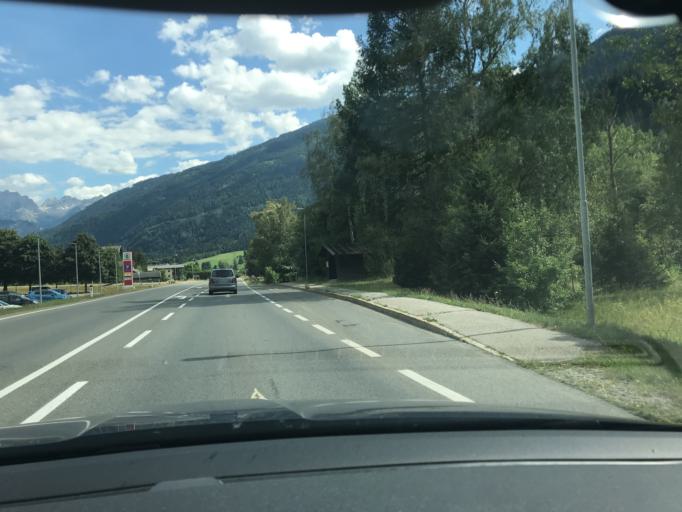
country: AT
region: Tyrol
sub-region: Politischer Bezirk Lienz
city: Ainet
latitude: 46.8665
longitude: 12.6867
